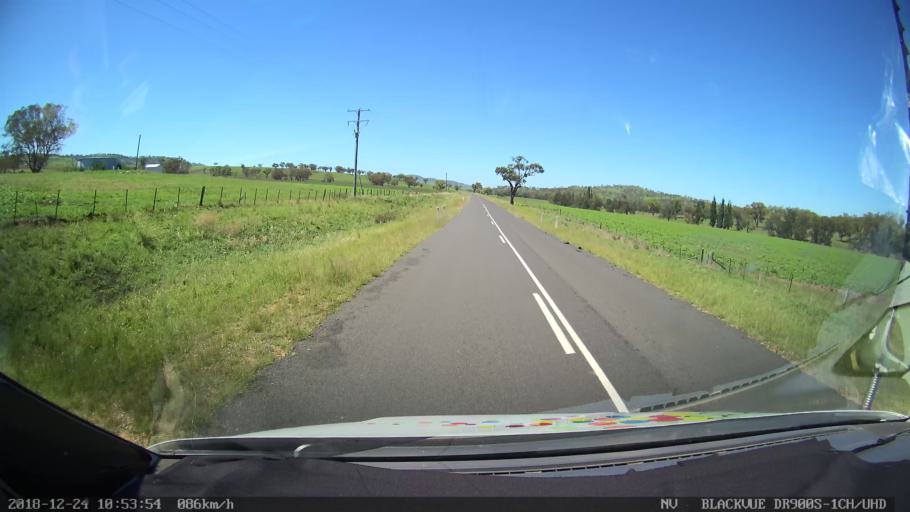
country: AU
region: New South Wales
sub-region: Upper Hunter Shire
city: Merriwa
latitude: -31.9971
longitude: 150.4190
